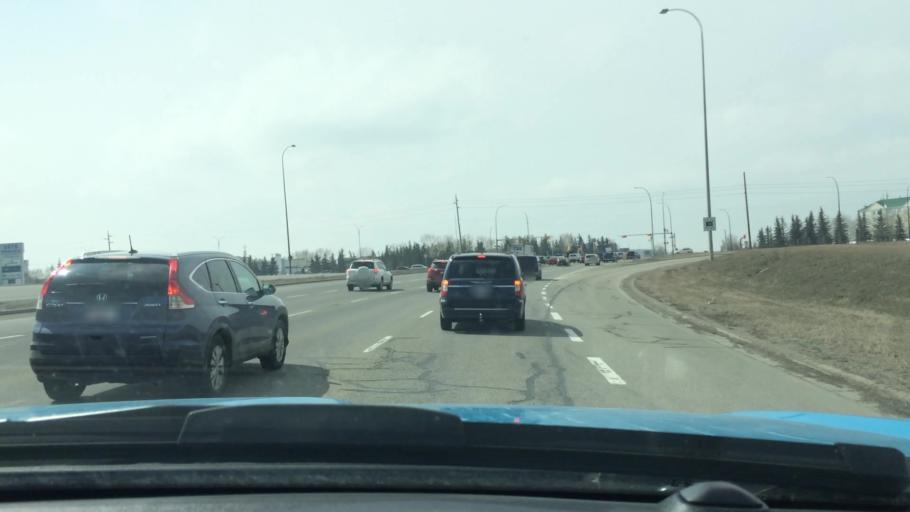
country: CA
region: Alberta
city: Calgary
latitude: 51.0932
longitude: -113.9984
